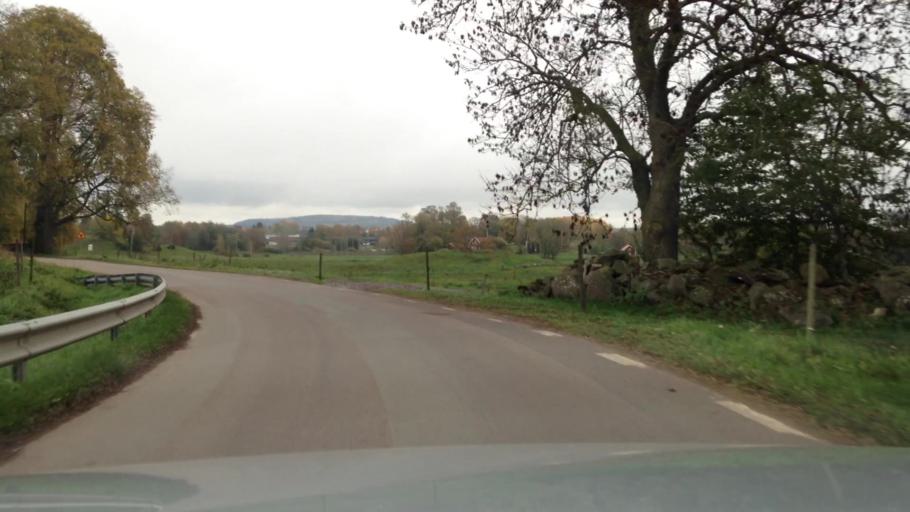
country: SE
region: Vaestra Goetaland
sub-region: Falkopings Kommun
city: Akarp
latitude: 58.2690
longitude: 13.6940
